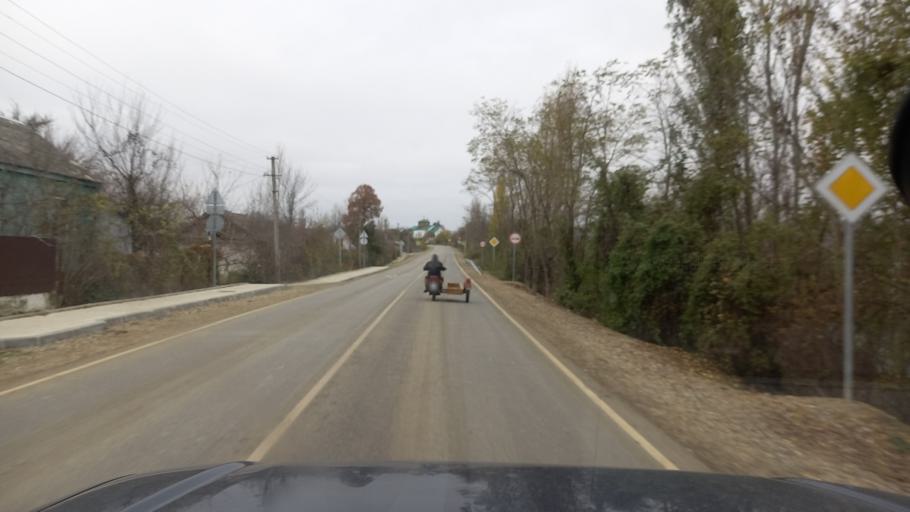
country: RU
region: Krasnodarskiy
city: Goryachiy Klyuch
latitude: 44.5225
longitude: 39.2930
